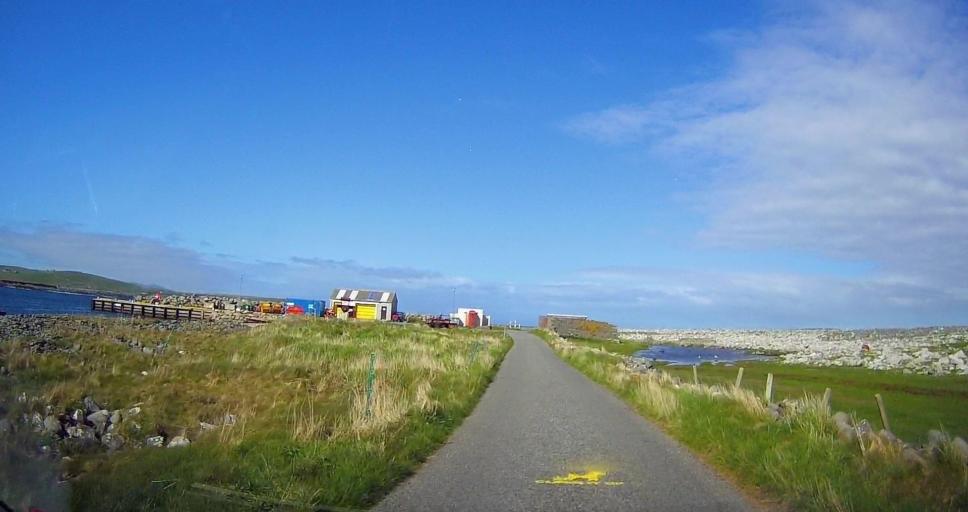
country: GB
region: Scotland
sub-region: Shetland Islands
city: Sandwick
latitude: 59.8733
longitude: -1.2783
